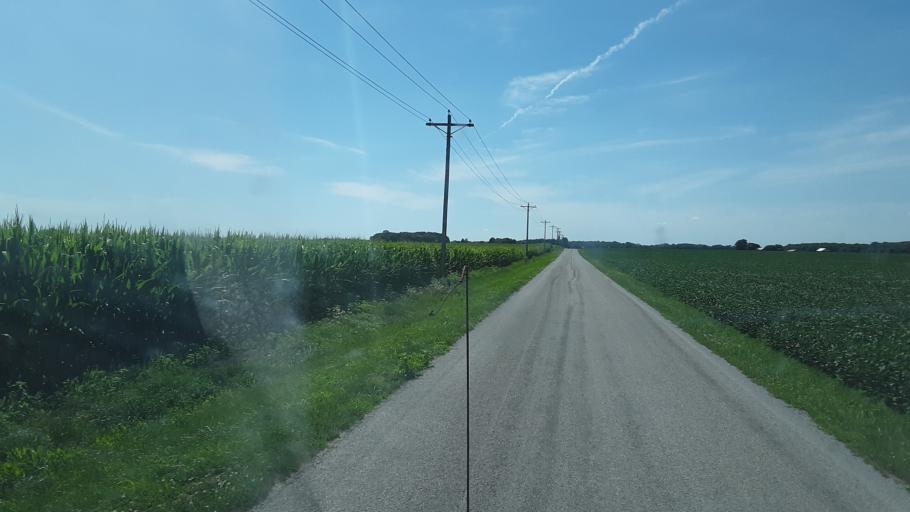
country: US
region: Ohio
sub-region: Marion County
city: Marion
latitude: 40.6582
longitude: -83.2817
